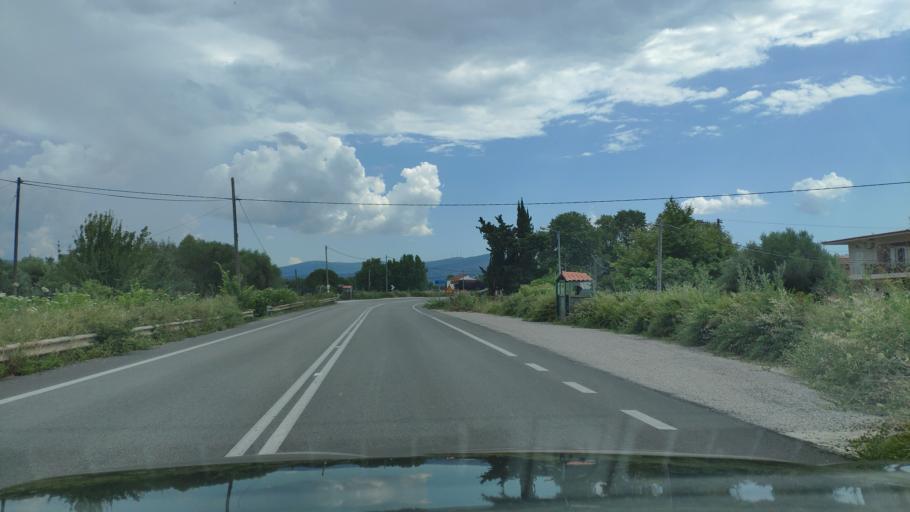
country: GR
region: West Greece
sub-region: Nomos Aitolias kai Akarnanias
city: Krikellos
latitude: 38.9208
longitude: 21.1788
